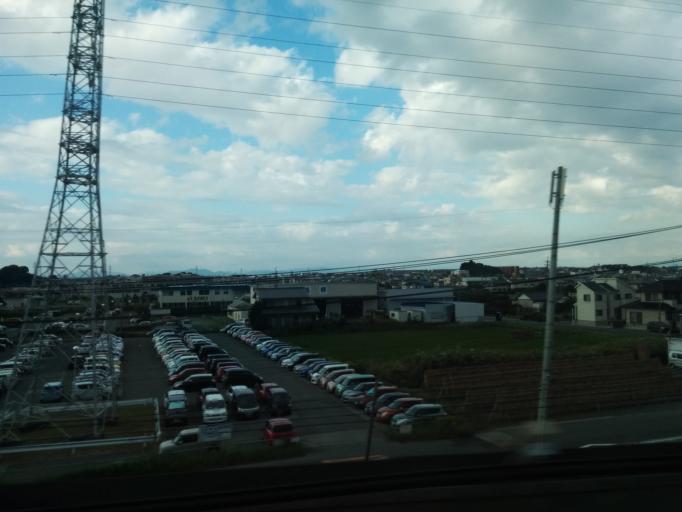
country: JP
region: Shizuoka
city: Hamamatsu
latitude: 34.6943
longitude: 137.6926
